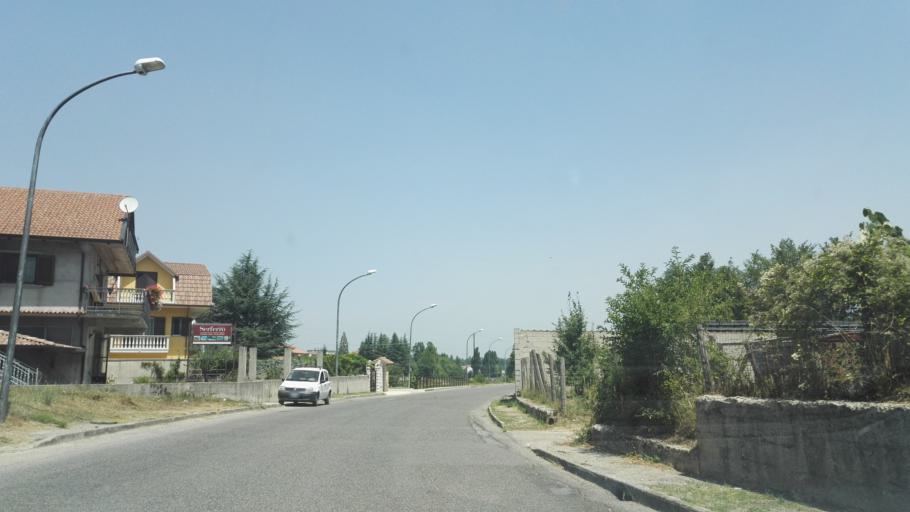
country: IT
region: Calabria
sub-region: Provincia di Vibo-Valentia
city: Serra San Bruno
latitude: 38.5684
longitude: 16.3277
